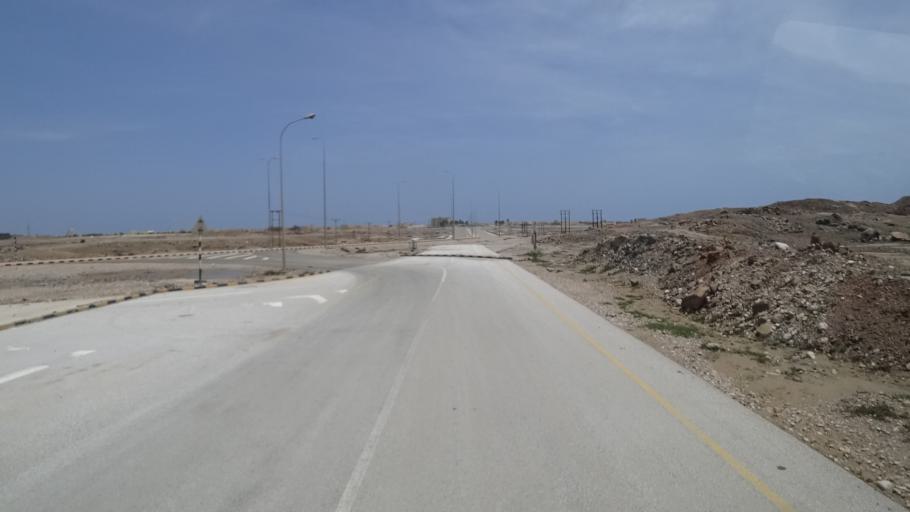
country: OM
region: Zufar
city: Salalah
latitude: 17.0067
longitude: 54.6976
